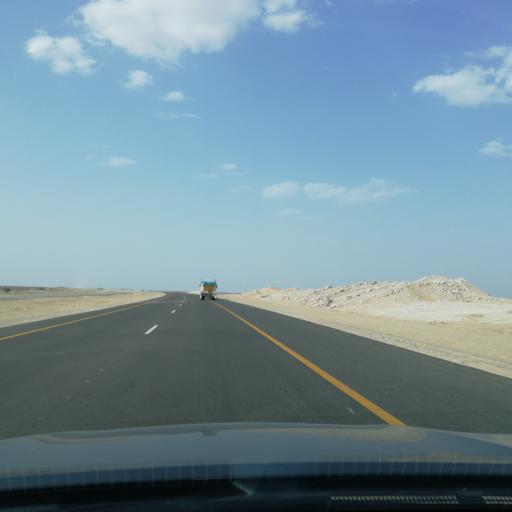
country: OM
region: Muhafazat ad Dakhiliyah
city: Adam
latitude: 22.0395
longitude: 57.5090
